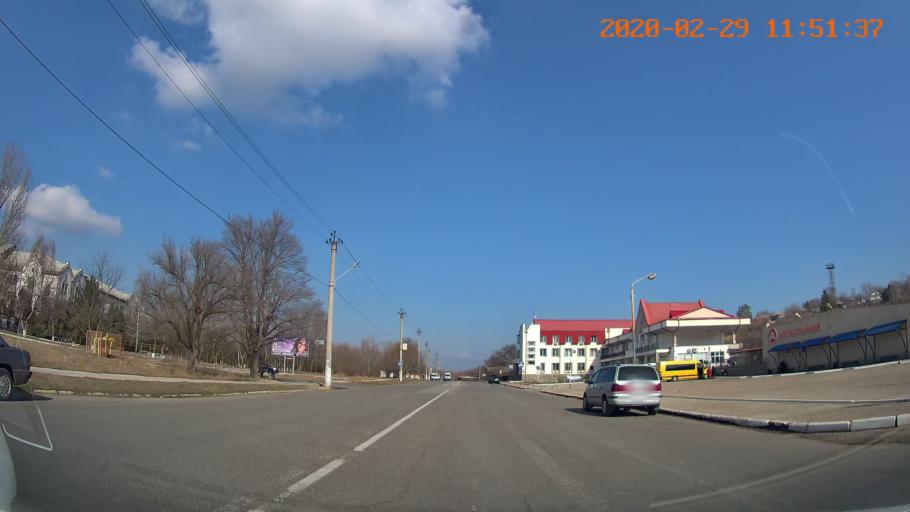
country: MD
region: Telenesti
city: Ribnita
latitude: 47.7655
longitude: 28.9903
